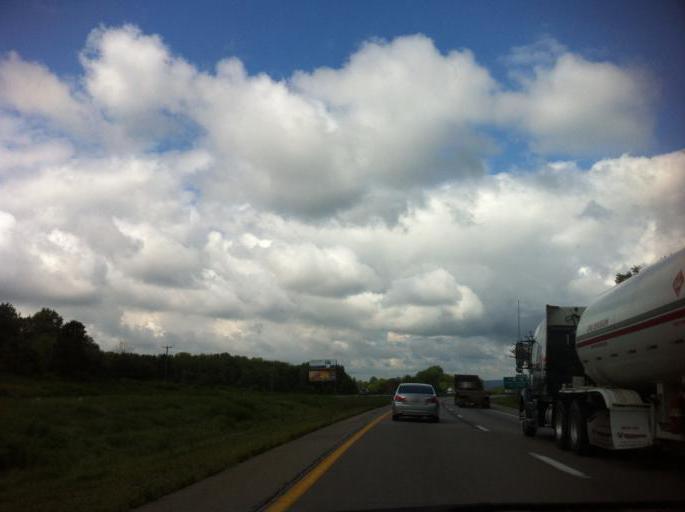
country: US
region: Pennsylvania
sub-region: Mercer County
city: Hermitage
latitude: 41.1829
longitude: -80.4171
